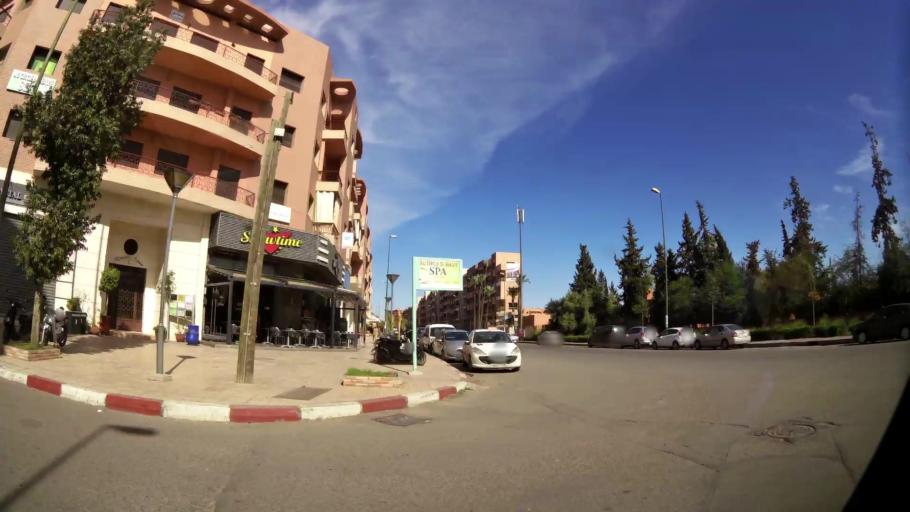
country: MA
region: Marrakech-Tensift-Al Haouz
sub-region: Marrakech
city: Marrakesh
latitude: 31.6491
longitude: -8.0122
